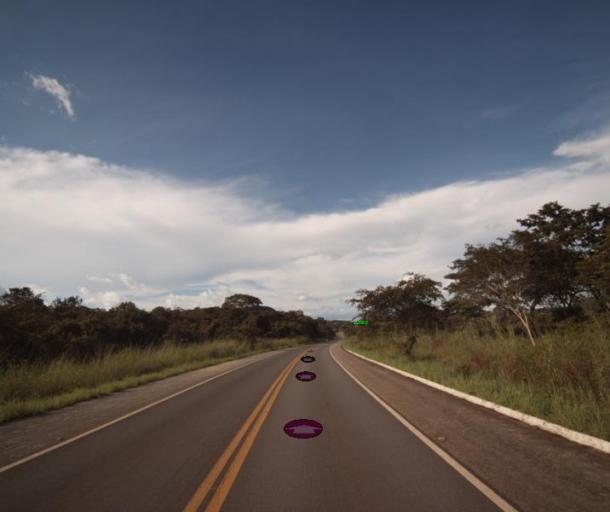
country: BR
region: Goias
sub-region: Barro Alto
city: Barro Alto
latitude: -14.9826
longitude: -48.6779
